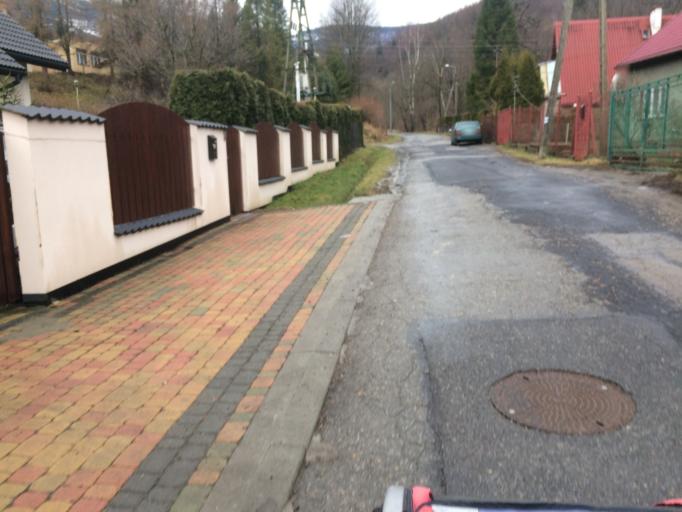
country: PL
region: Silesian Voivodeship
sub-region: Powiat bielski
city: Bystra
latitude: 49.7575
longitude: 19.0269
